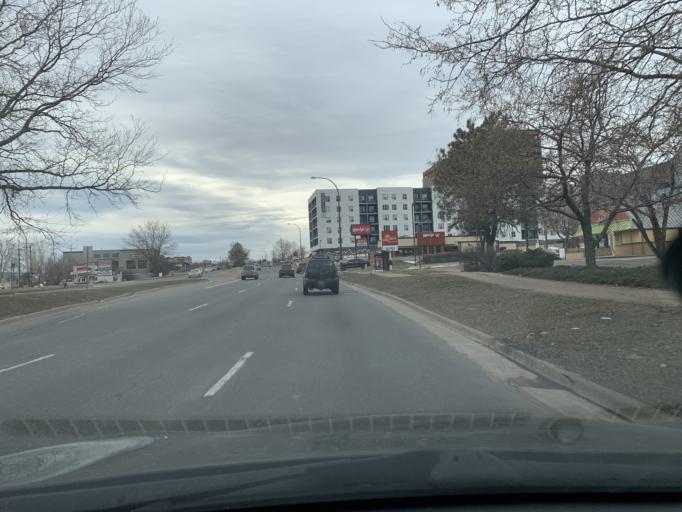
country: US
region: Colorado
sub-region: Jefferson County
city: West Pleasant View
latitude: 39.7154
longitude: -105.1334
